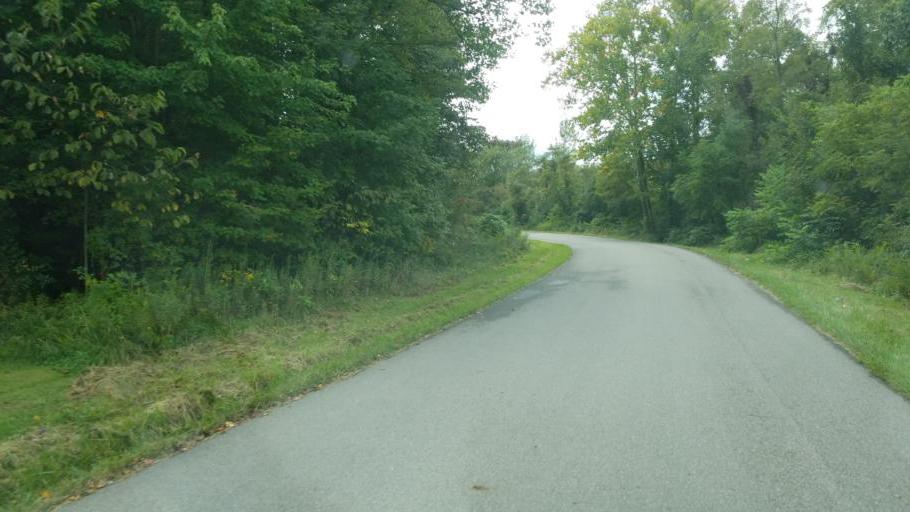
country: US
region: Ohio
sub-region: Jackson County
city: Oak Hill
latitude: 38.9020
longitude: -82.6166
